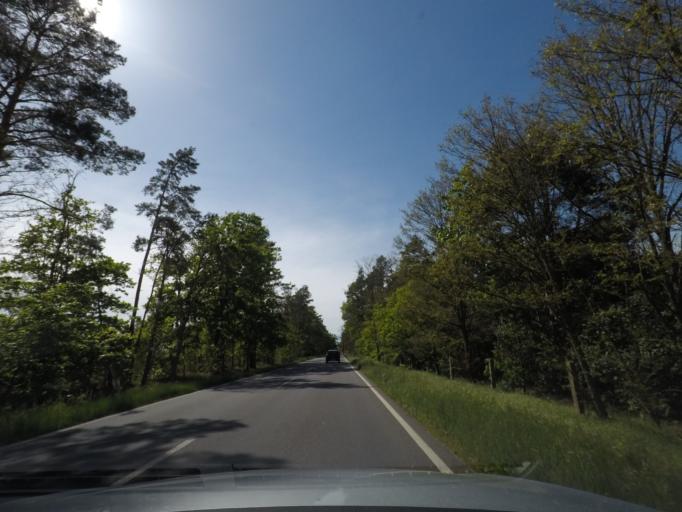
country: DE
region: Brandenburg
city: Luebben
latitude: 51.9493
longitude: 13.7953
